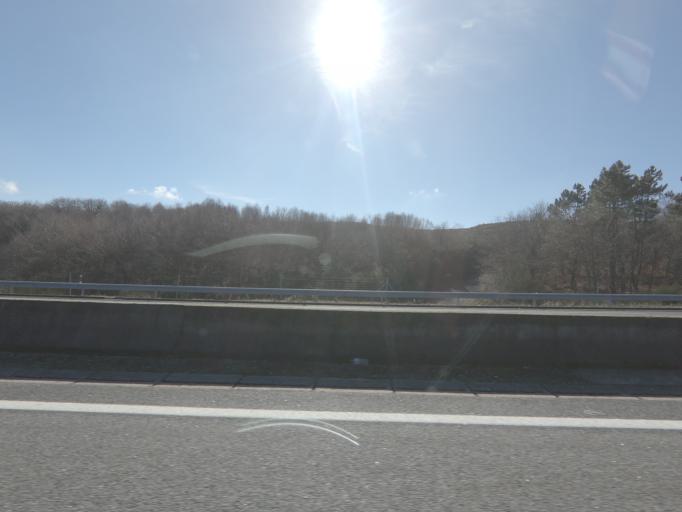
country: ES
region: Galicia
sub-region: Provincia de Pontevedra
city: Dozon
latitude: 42.5563
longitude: -8.0230
